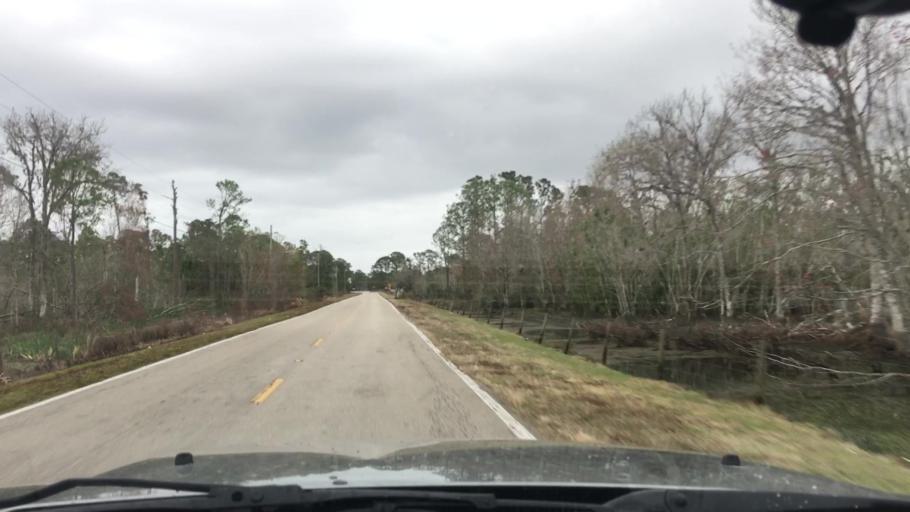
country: US
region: Florida
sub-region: Highlands County
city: Sebring
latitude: 27.4459
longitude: -81.4505
